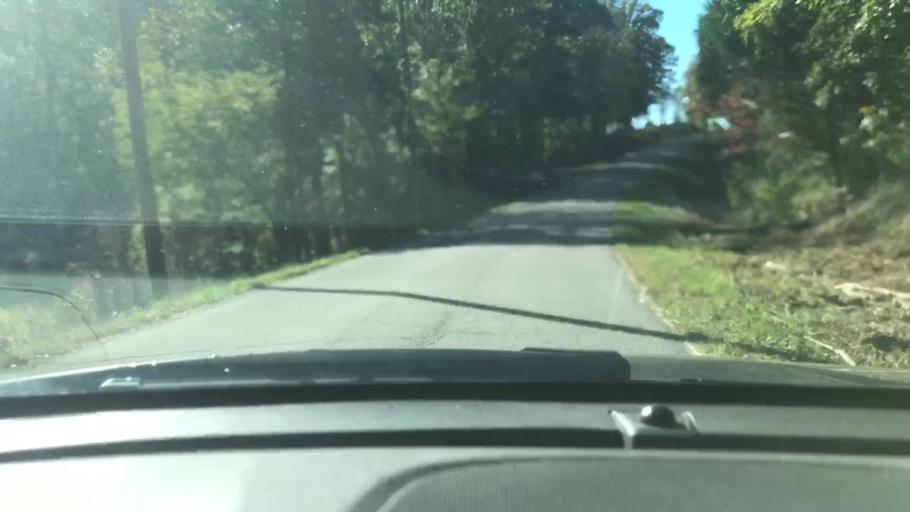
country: US
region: Tennessee
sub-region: Dickson County
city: Charlotte
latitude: 36.1800
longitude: -87.2912
